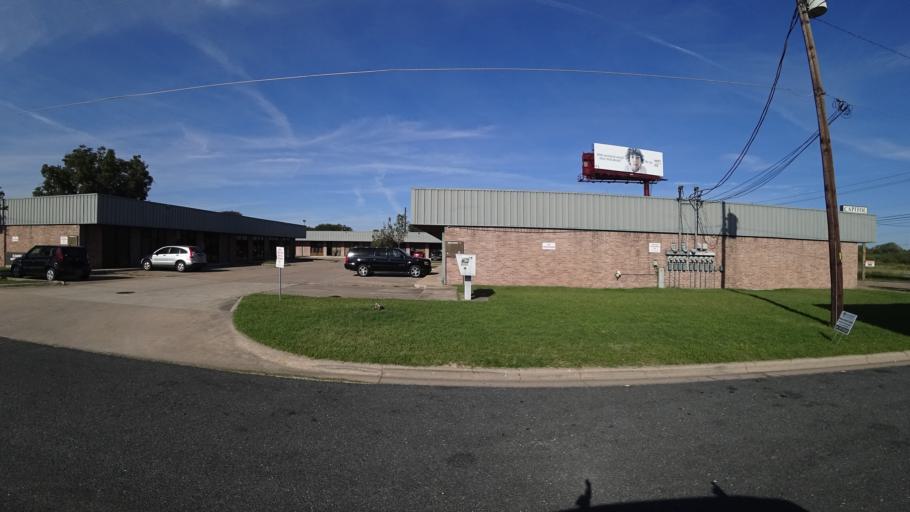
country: US
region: Texas
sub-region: Travis County
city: Austin
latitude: 30.2572
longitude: -97.6778
